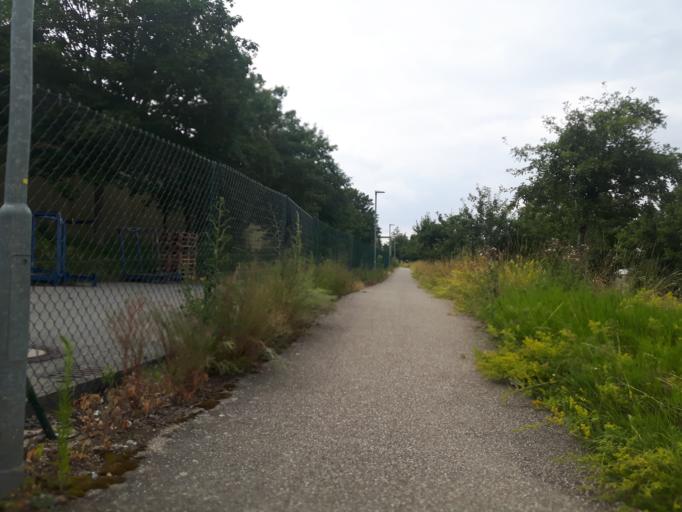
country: DE
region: Baden-Wuerttemberg
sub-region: Regierungsbezirk Stuttgart
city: Brackenheim
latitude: 49.0809
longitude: 9.0963
